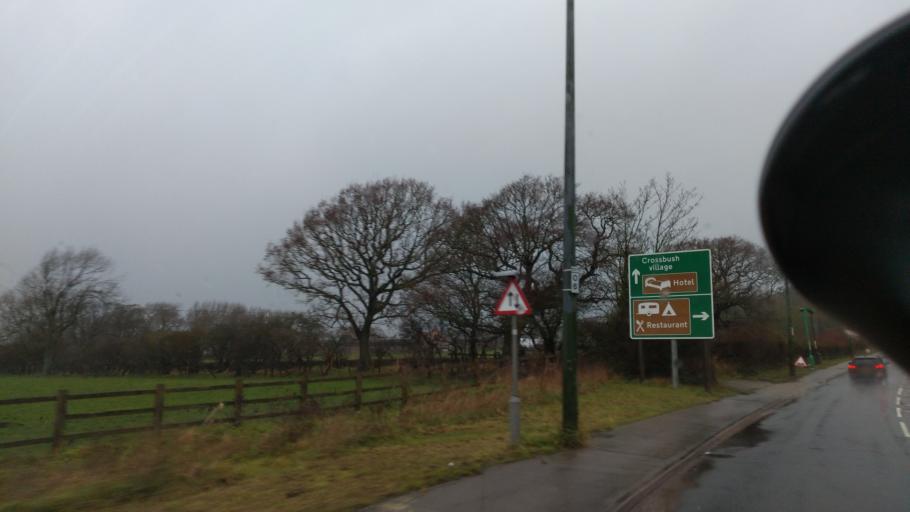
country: GB
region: England
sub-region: West Sussex
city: Arundel
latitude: 50.8443
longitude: -0.5409
